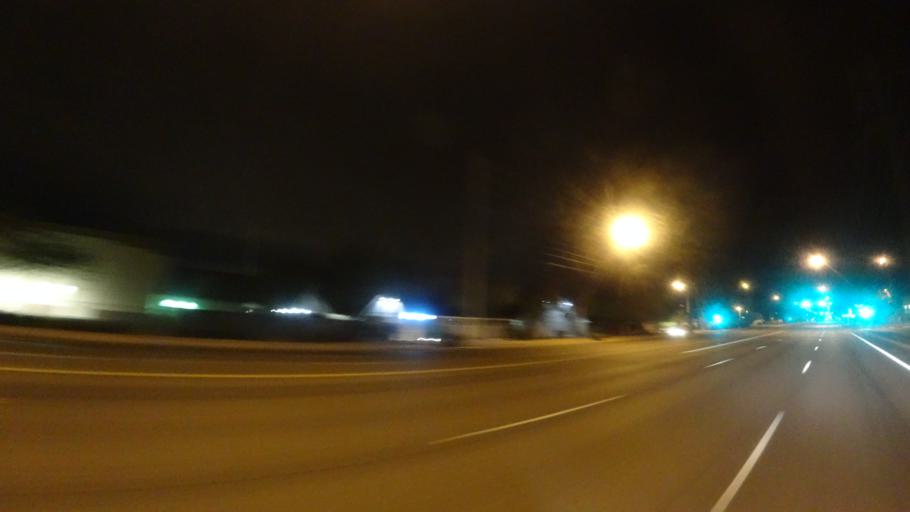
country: US
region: Arizona
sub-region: Maricopa County
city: Gilbert
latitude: 33.4292
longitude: -111.6843
